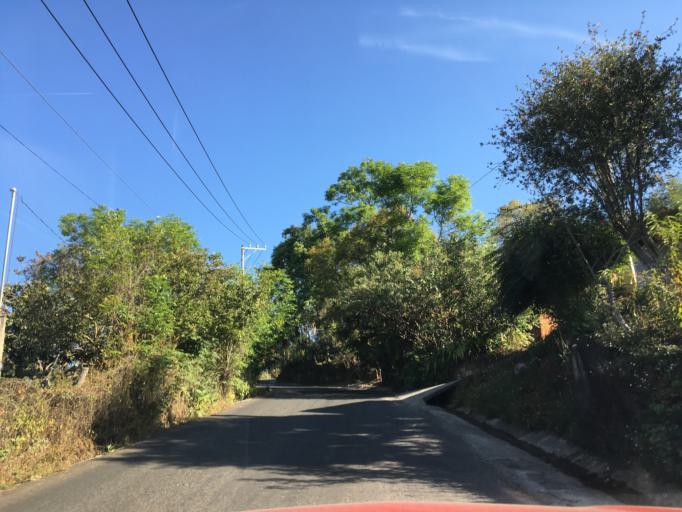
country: MX
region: Michoacan
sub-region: Zitacuaro
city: Valle Verde
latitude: 19.4703
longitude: -100.3439
